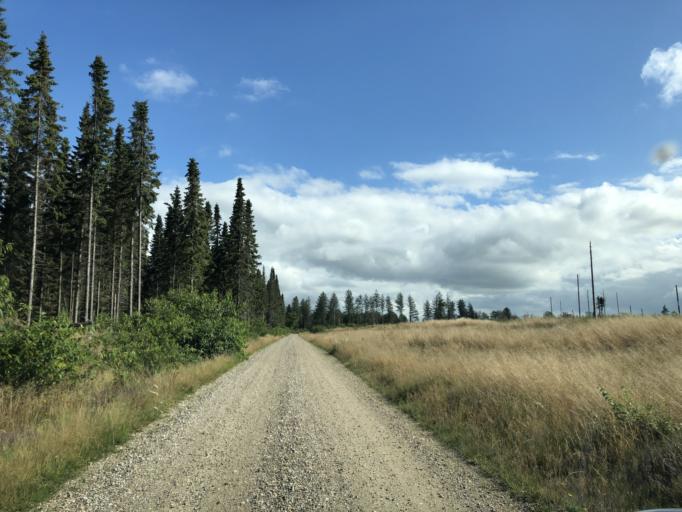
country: DK
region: Central Jutland
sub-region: Holstebro Kommune
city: Ulfborg
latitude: 56.2472
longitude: 8.4855
